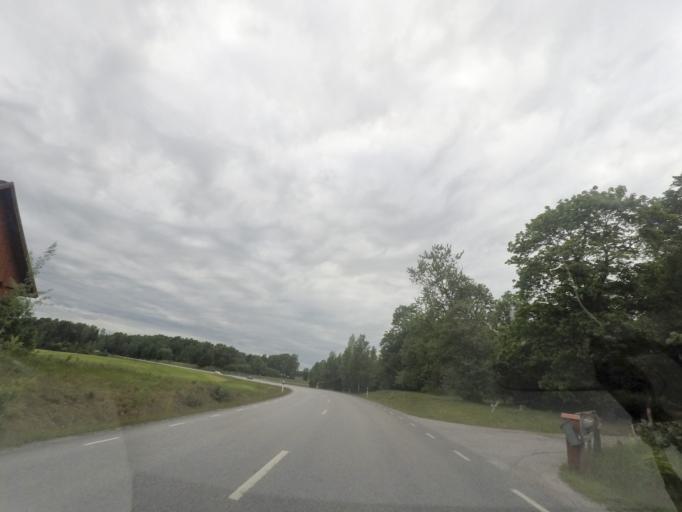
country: SE
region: Vaestmanland
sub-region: Arboga Kommun
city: Arboga
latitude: 59.4125
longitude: 15.7854
